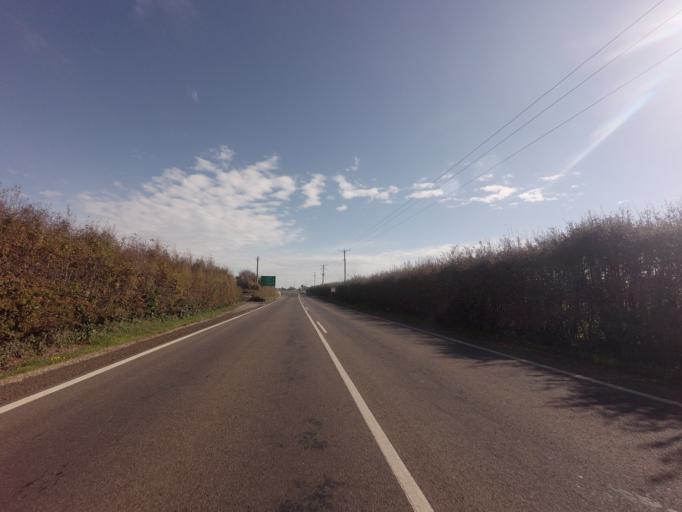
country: AU
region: Tasmania
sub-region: Meander Valley
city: Westbury
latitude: -41.5261
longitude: 146.8785
